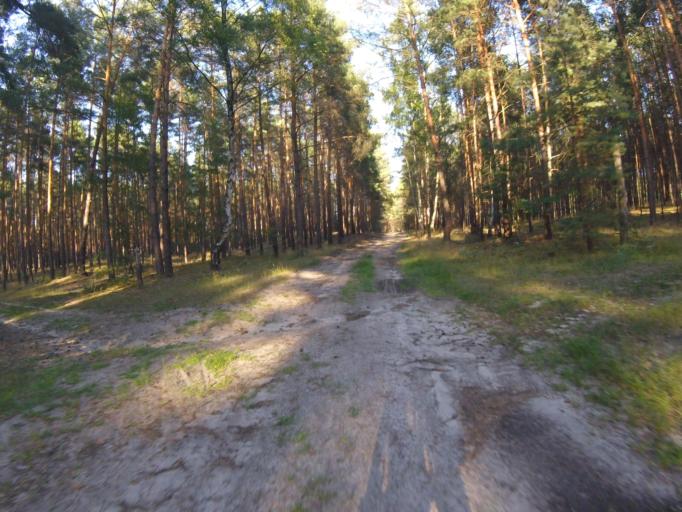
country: DE
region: Brandenburg
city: Teupitz
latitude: 52.1595
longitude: 13.5958
